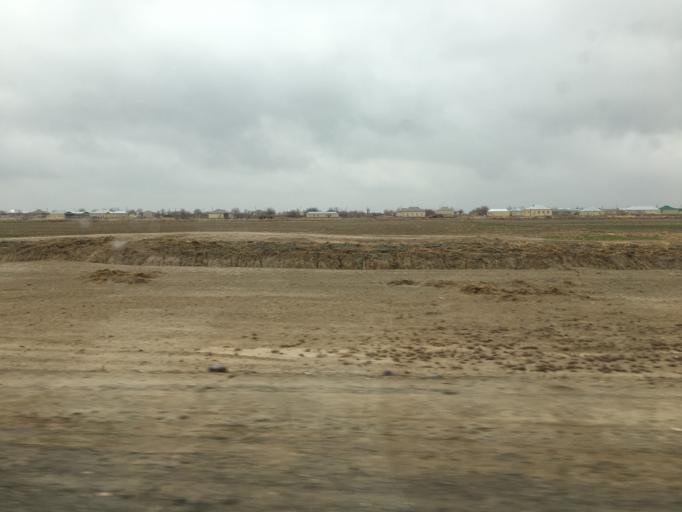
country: TM
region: Mary
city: Yoloeten
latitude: 37.4005
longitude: 62.1767
